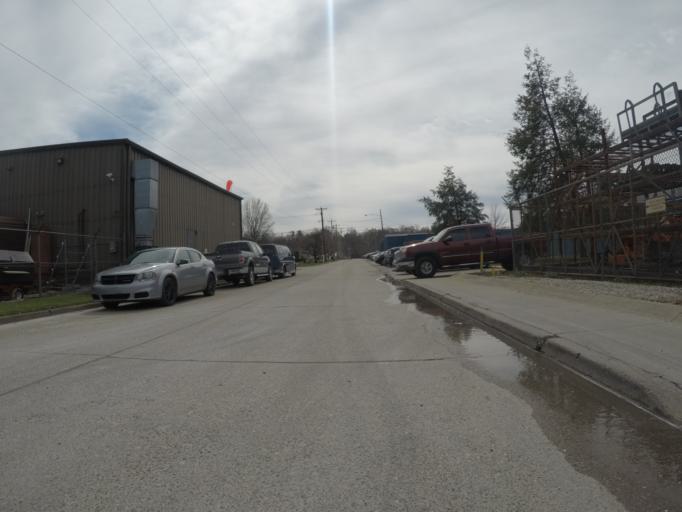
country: US
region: West Virginia
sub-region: Cabell County
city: Pea Ridge
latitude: 38.4162
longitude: -82.3694
